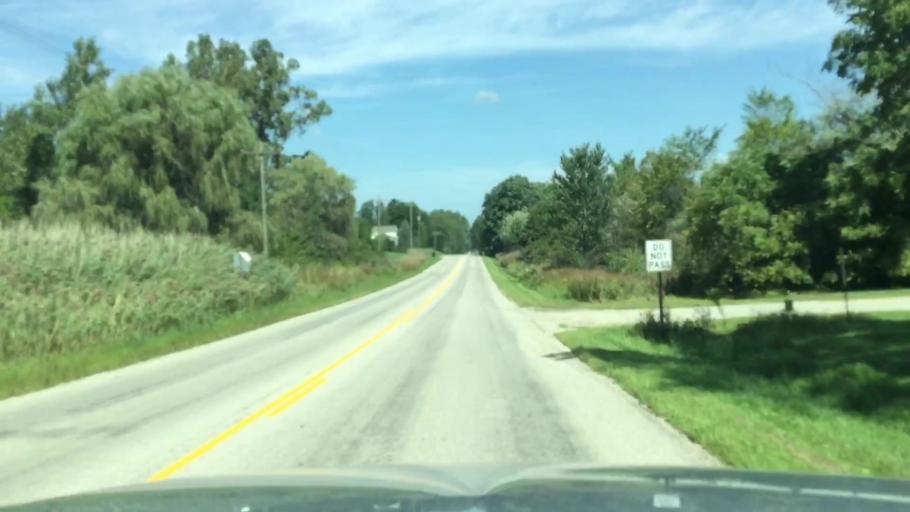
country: US
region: Michigan
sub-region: Lenawee County
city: Manitou Beach-Devils Lake
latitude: 42.0194
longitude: -84.2762
